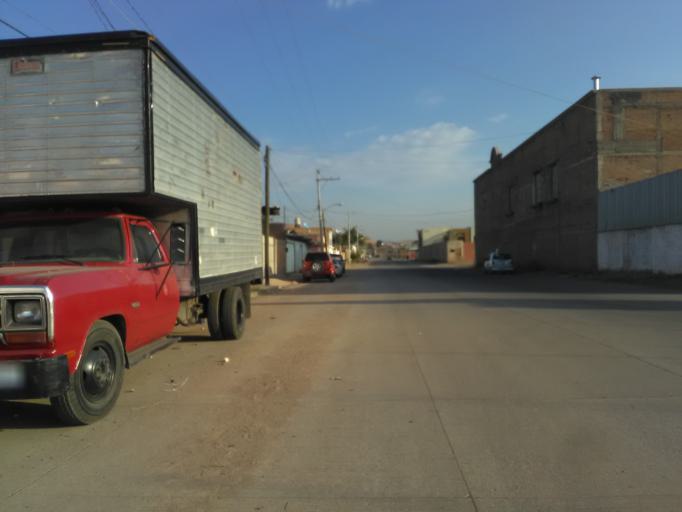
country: MX
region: Durango
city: Victoria de Durango
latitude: 24.0510
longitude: -104.6484
